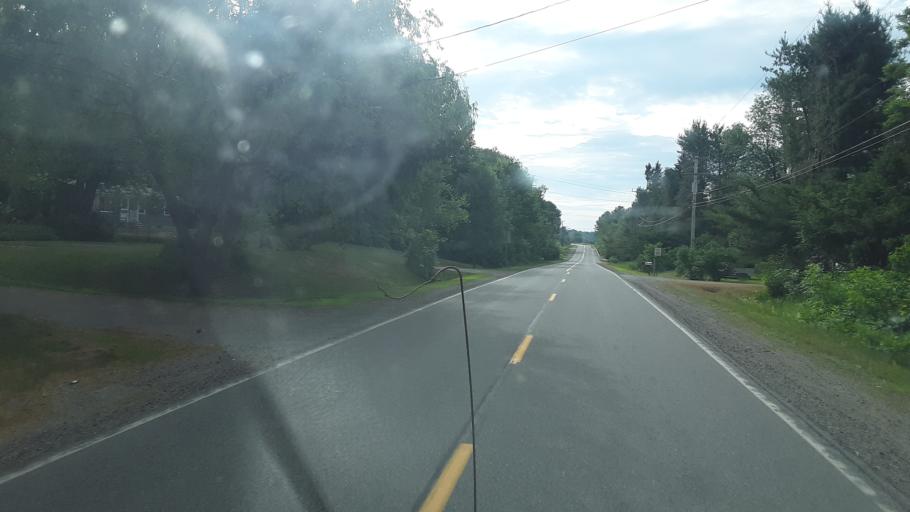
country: US
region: Maine
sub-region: Penobscot County
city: Medway
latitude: 45.5967
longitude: -68.4986
